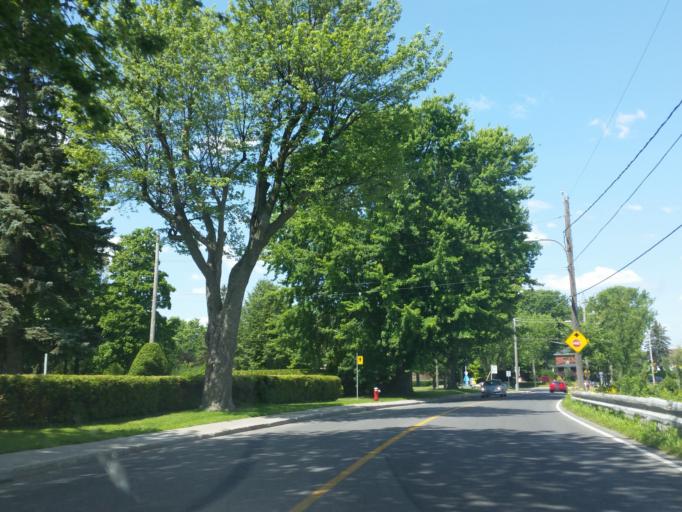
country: CA
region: Quebec
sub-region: Monteregie
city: Saint-Jean-sur-Richelieu
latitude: 45.3197
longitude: -73.2603
